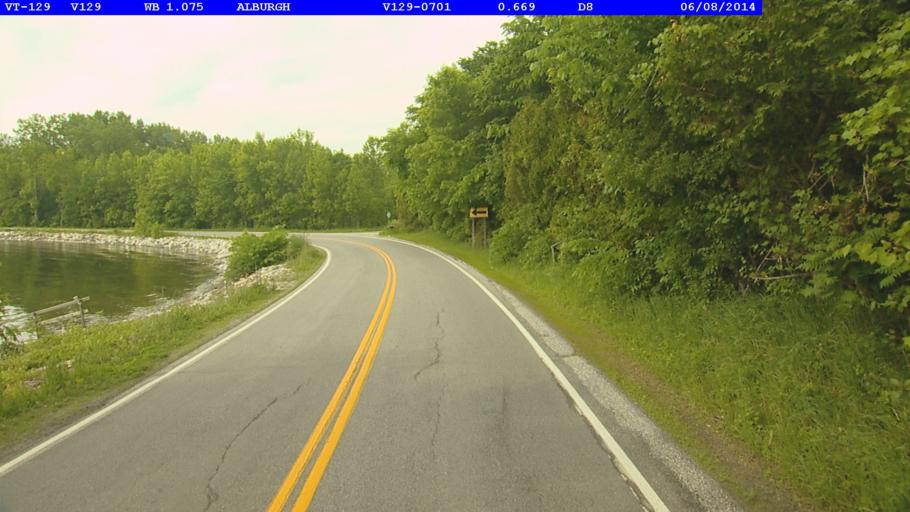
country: US
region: Vermont
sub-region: Grand Isle County
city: North Hero
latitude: 44.9019
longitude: -73.3041
